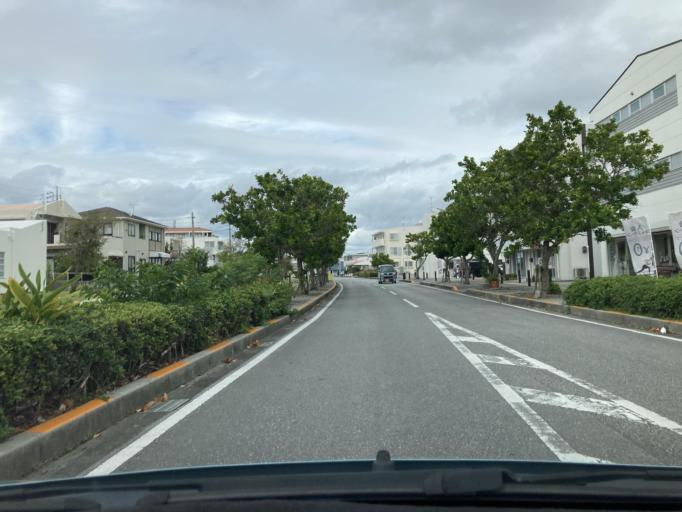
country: JP
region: Okinawa
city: Itoman
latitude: 26.1536
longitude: 127.6627
